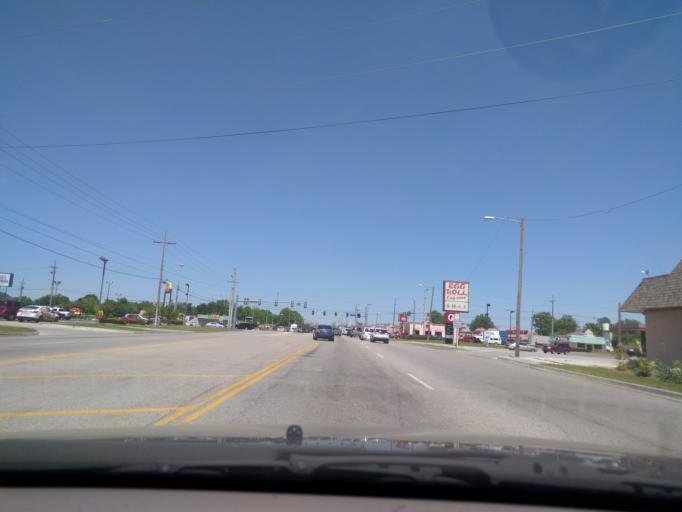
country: US
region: Oklahoma
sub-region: Tulsa County
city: Broken Arrow
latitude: 36.0597
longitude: -95.7974
